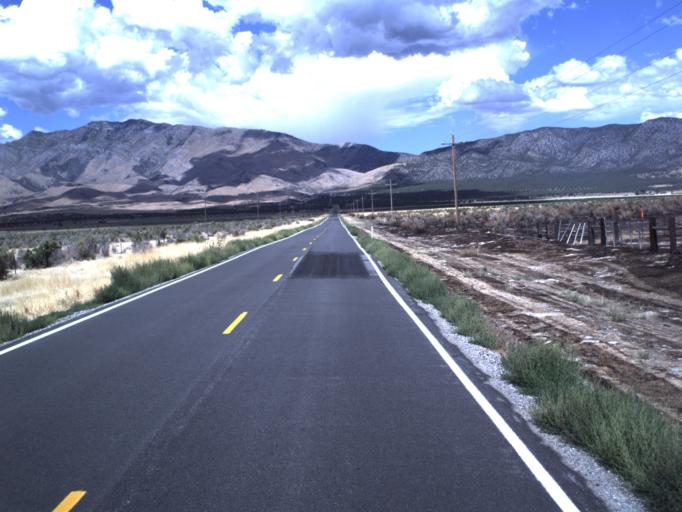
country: US
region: Utah
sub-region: Tooele County
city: Grantsville
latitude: 40.2881
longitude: -112.6624
